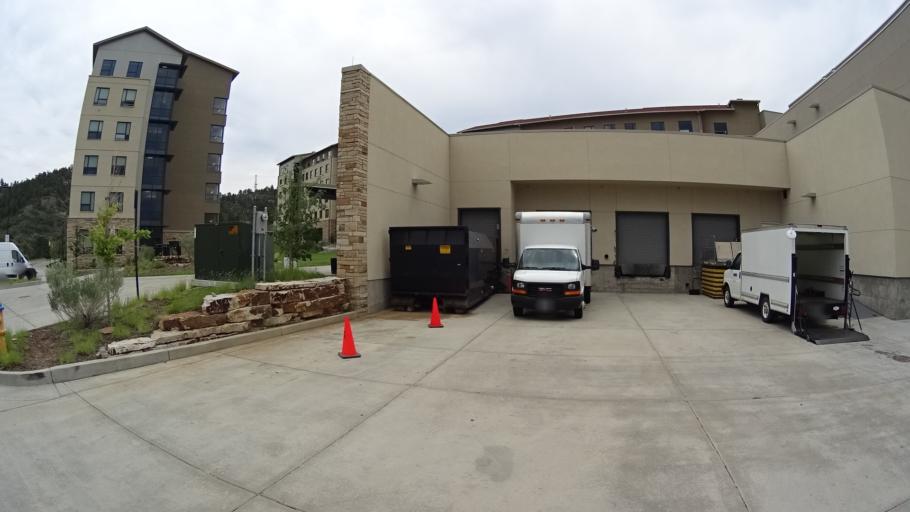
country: US
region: Colorado
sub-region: El Paso County
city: Colorado Springs
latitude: 38.8988
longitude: -104.8053
